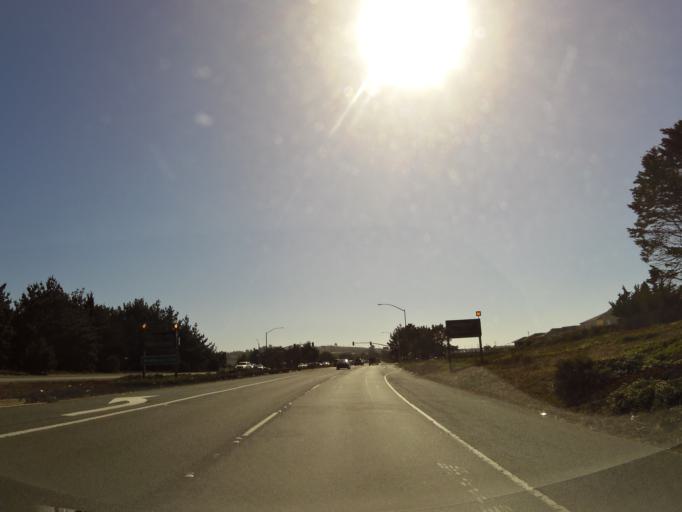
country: US
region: California
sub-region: San Mateo County
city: Broadmoor
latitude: 37.6847
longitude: -122.4891
